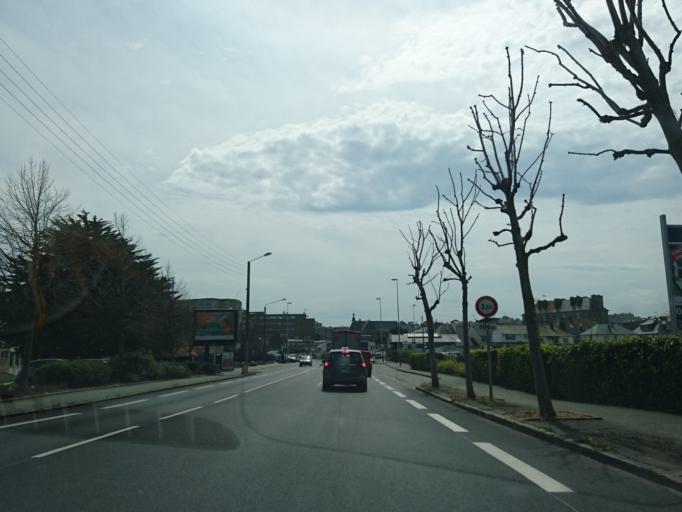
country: FR
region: Brittany
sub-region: Departement d'Ille-et-Vilaine
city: Saint-Malo
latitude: 48.6411
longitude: -2.0087
